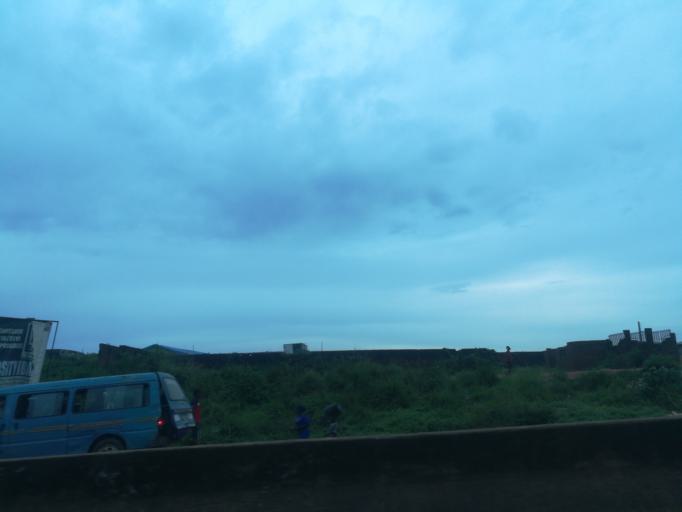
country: NG
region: Oyo
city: Ibadan
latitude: 7.3973
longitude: 3.9516
